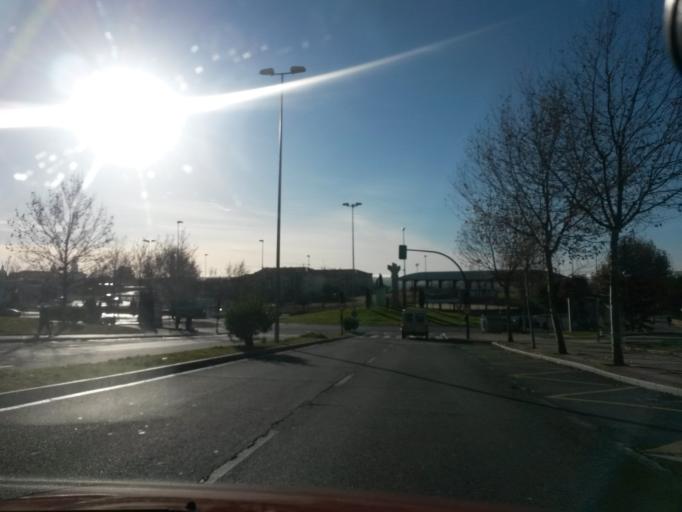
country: ES
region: Castille and Leon
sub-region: Provincia de Salamanca
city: Salamanca
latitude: 40.9729
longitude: -5.6811
